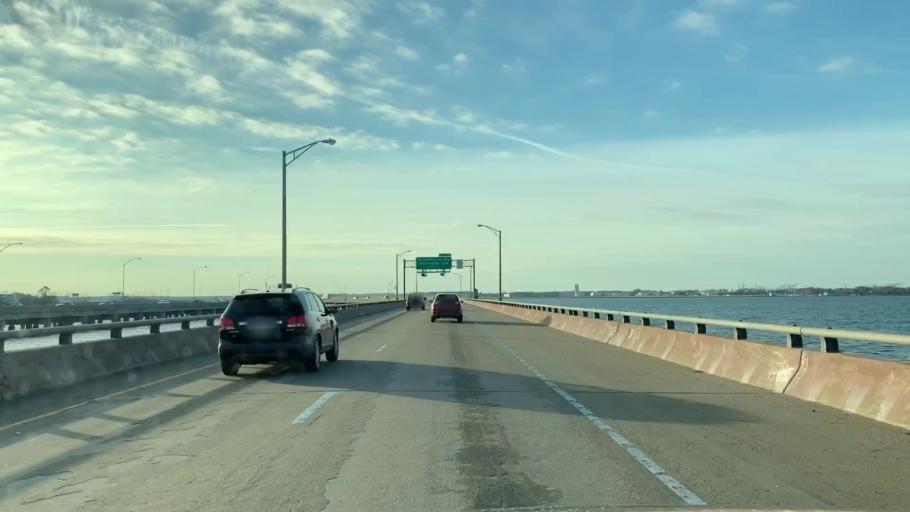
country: US
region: Virginia
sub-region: City of Hampton
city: East Hampton
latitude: 36.9734
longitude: -76.3008
